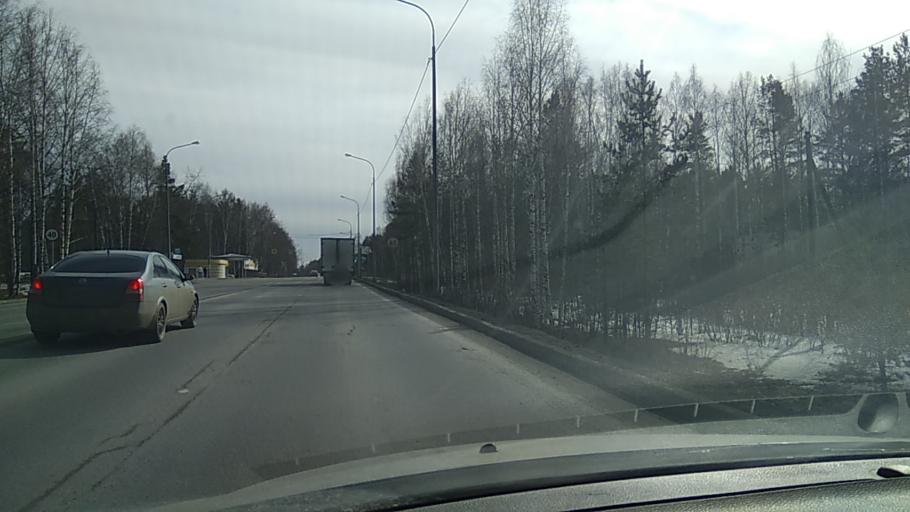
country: RU
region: Sverdlovsk
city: Nikolo-Pavlovskoye
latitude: 57.8547
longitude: 60.0315
